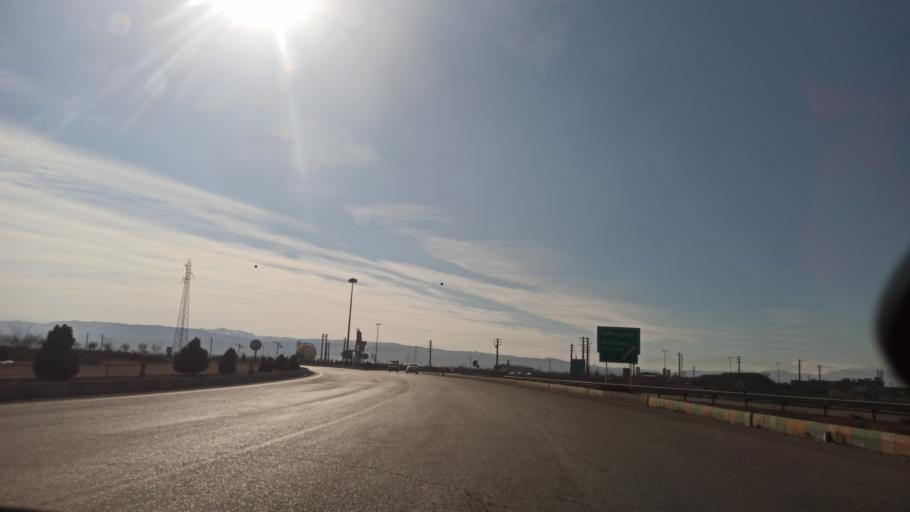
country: IR
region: Qazvin
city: Bu'in Zahra
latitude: 35.7681
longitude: 50.0839
